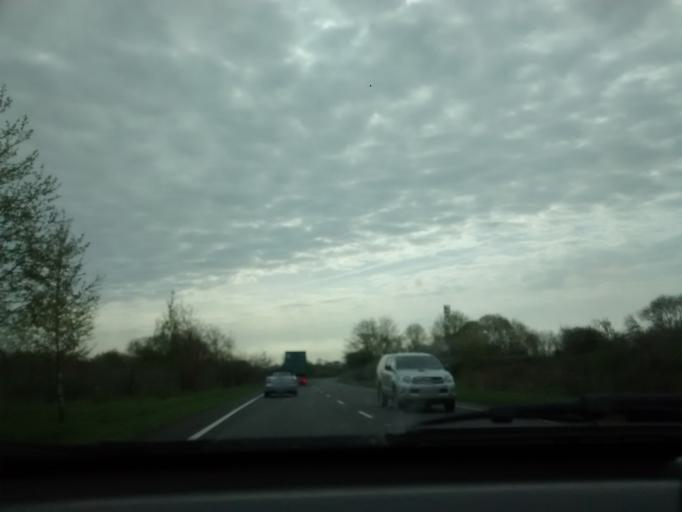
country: GB
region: England
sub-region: Oxfordshire
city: Bicester
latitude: 51.9097
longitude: -1.1335
